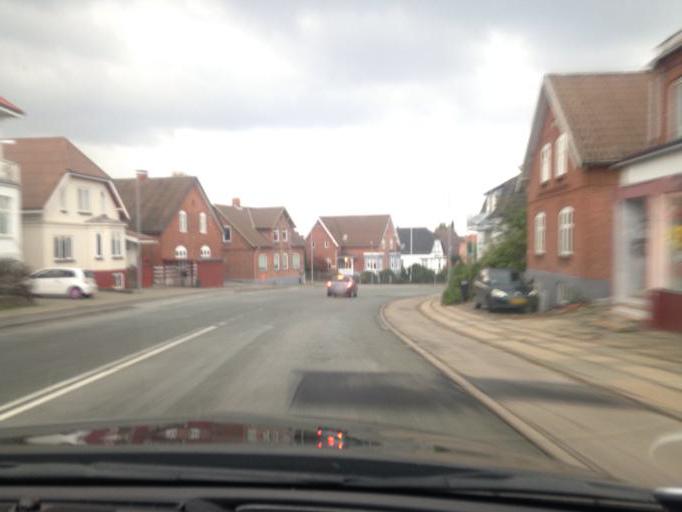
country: DK
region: South Denmark
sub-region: Kolding Kommune
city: Kolding
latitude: 55.4808
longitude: 9.4684
